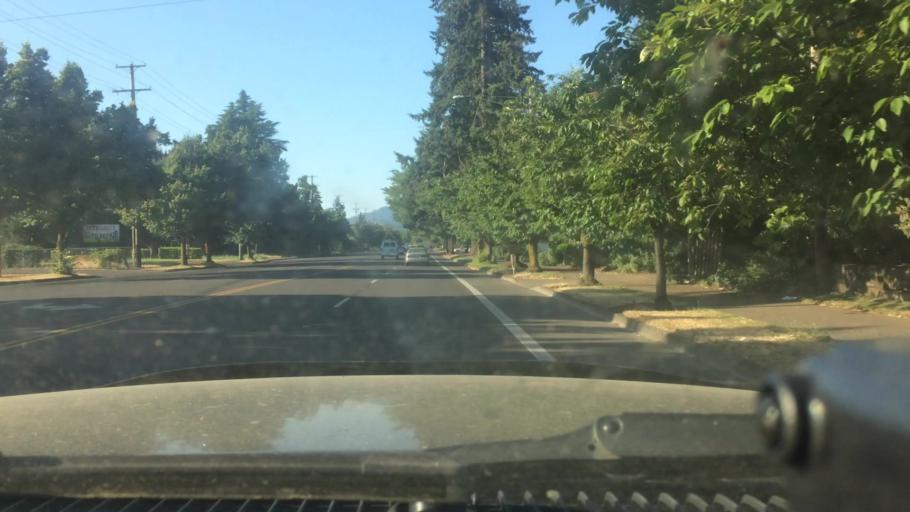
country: US
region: Oregon
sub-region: Lane County
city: Eugene
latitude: 44.0702
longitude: -123.1185
